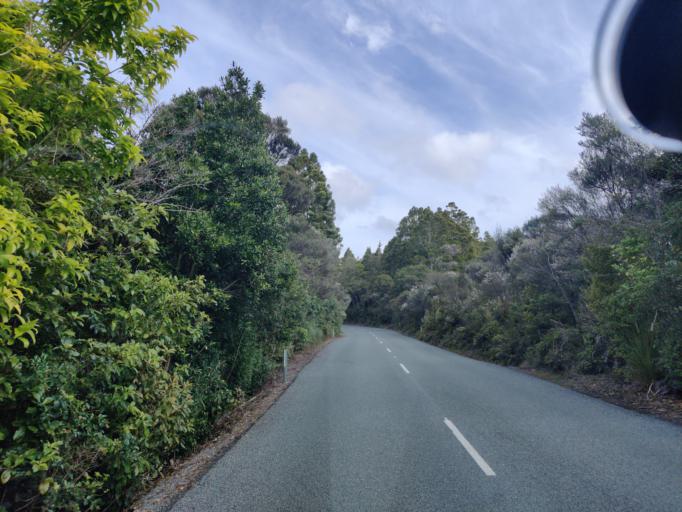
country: NZ
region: Northland
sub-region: Far North District
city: Waimate North
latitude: -35.6077
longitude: 173.5386
